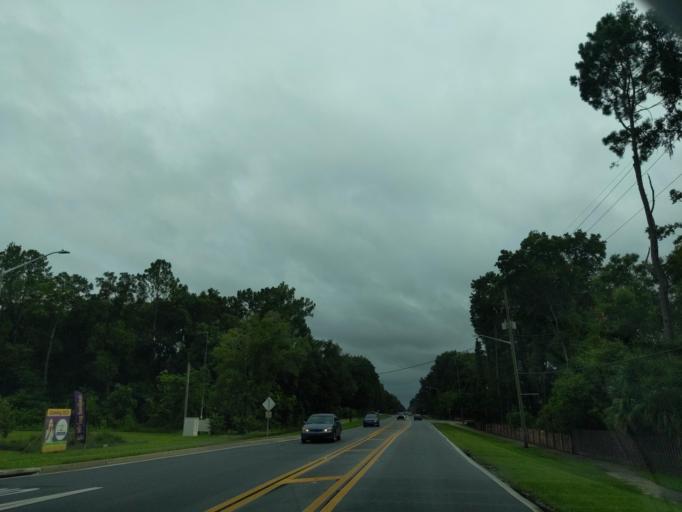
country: US
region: Florida
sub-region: Alachua County
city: Gainesville
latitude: 29.6374
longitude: -82.4225
